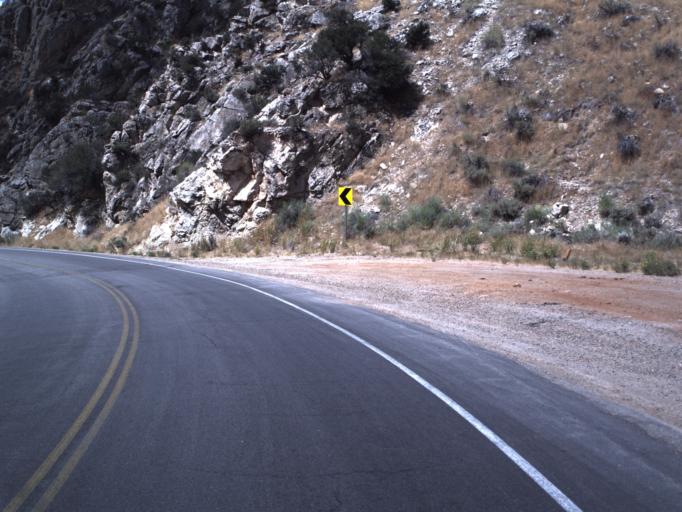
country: US
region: Utah
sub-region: Rich County
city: Randolph
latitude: 41.8248
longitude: -111.2933
